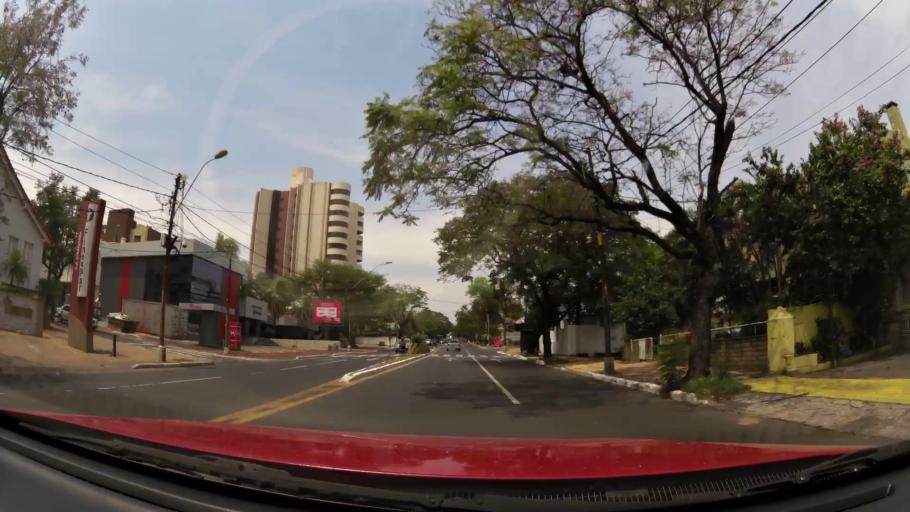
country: PY
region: Asuncion
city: Asuncion
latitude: -25.2913
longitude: -57.6161
